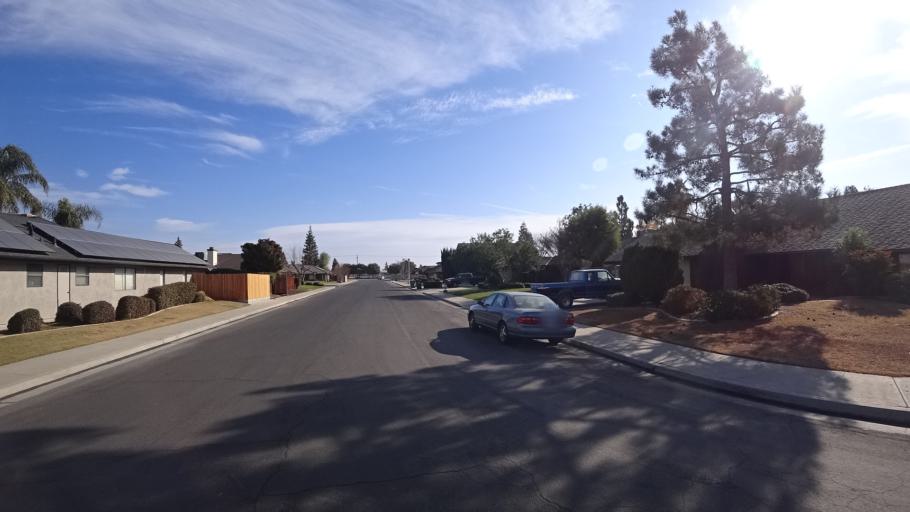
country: US
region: California
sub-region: Kern County
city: Greenacres
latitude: 35.4064
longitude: -119.0765
